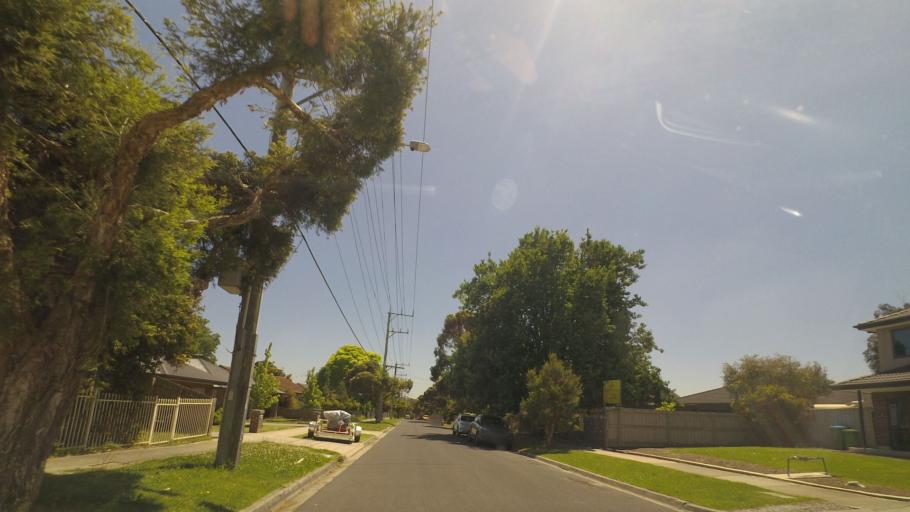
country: AU
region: Victoria
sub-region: Maroondah
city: Croydon North
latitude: -37.7701
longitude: 145.2941
